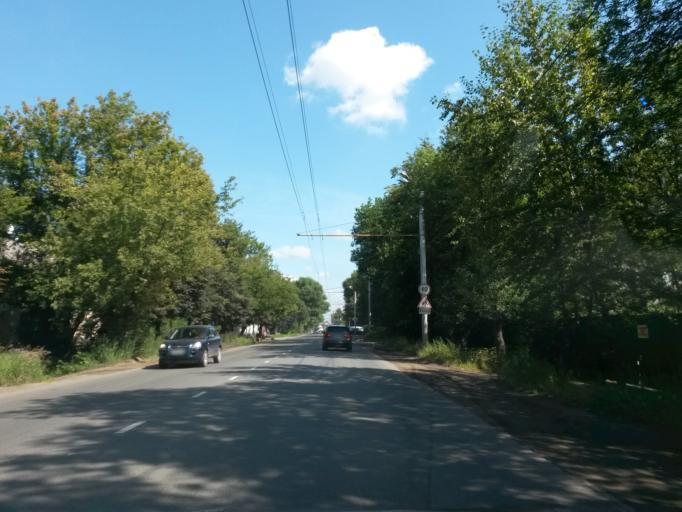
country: RU
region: Ivanovo
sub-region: Gorod Ivanovo
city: Ivanovo
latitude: 57.0049
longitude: 40.9474
